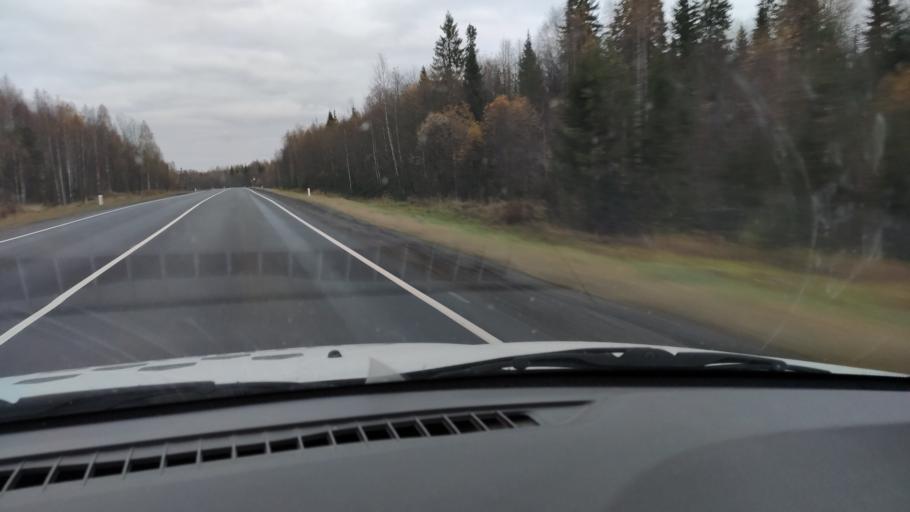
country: RU
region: Kirov
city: Lesnyye Polyany
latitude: 58.8017
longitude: 52.5735
